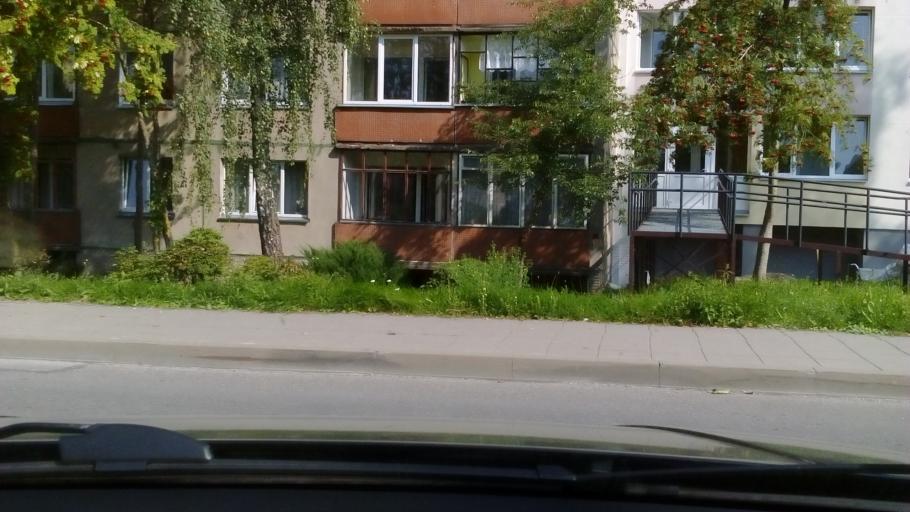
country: LT
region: Alytaus apskritis
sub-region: Alytus
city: Alytus
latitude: 54.3917
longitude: 24.0238
